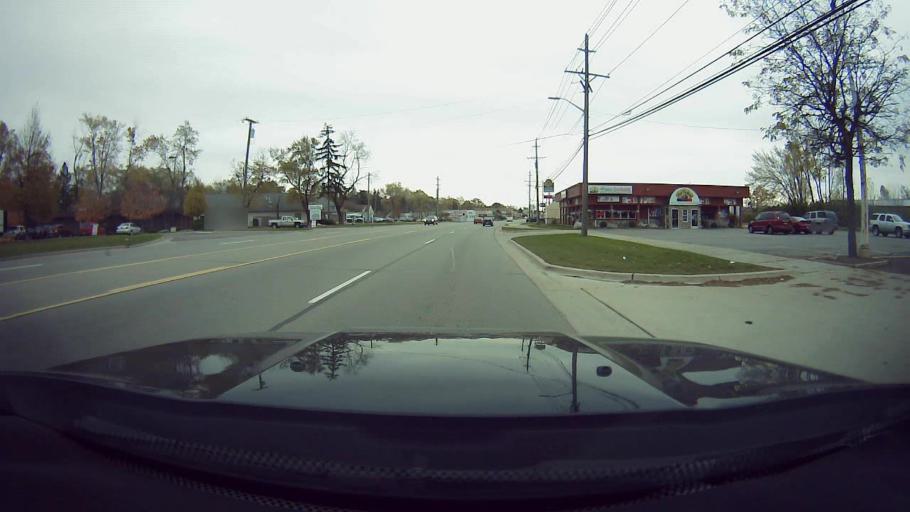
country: US
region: Michigan
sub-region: Oakland County
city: Pontiac
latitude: 42.6744
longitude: -83.3419
